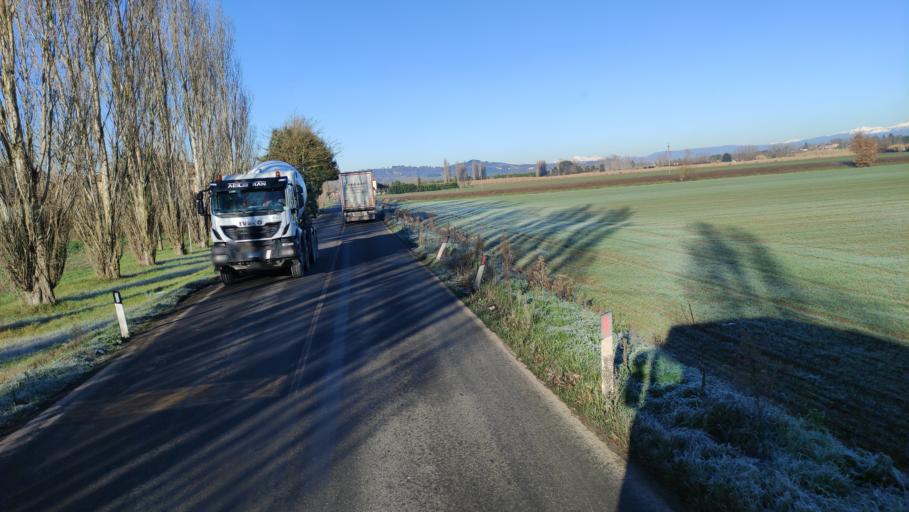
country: IT
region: Tuscany
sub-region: Province of Florence
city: Castelfiorentino
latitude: 43.6469
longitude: 10.9456
